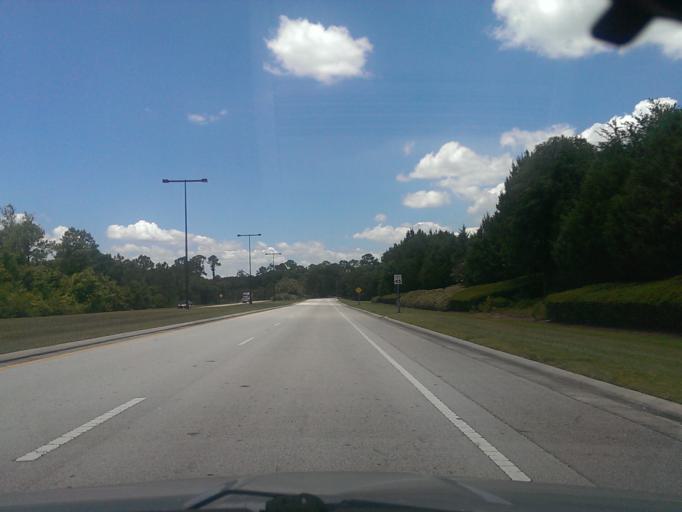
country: US
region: Florida
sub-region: Polk County
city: Citrus Ridge
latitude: 28.3755
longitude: -81.5993
